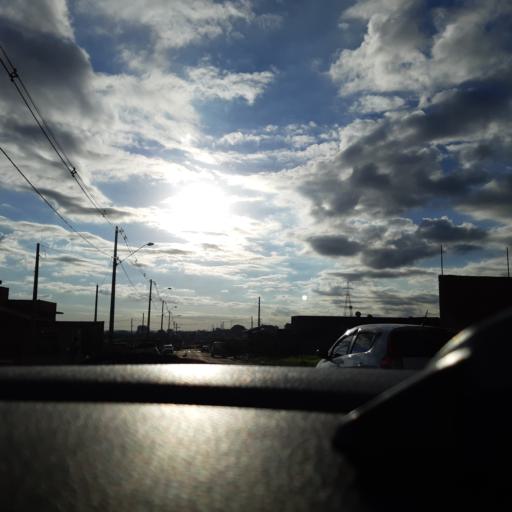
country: BR
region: Sao Paulo
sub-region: Ourinhos
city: Ourinhos
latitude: -23.0030
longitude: -49.8403
